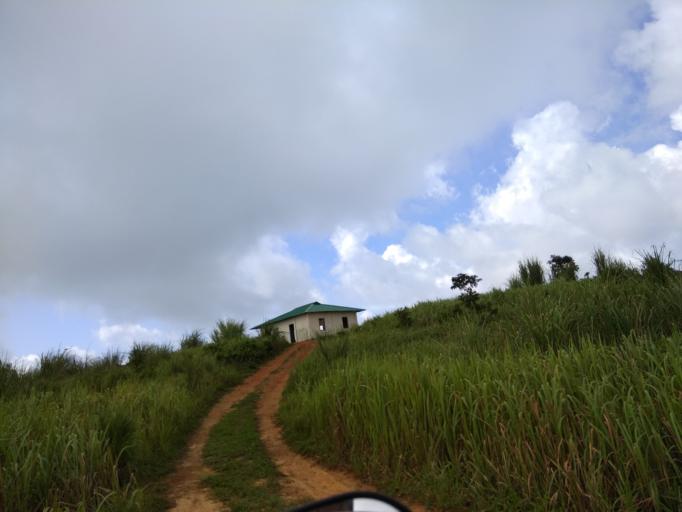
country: BD
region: Chittagong
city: Bandarban
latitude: 21.7439
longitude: 92.4178
